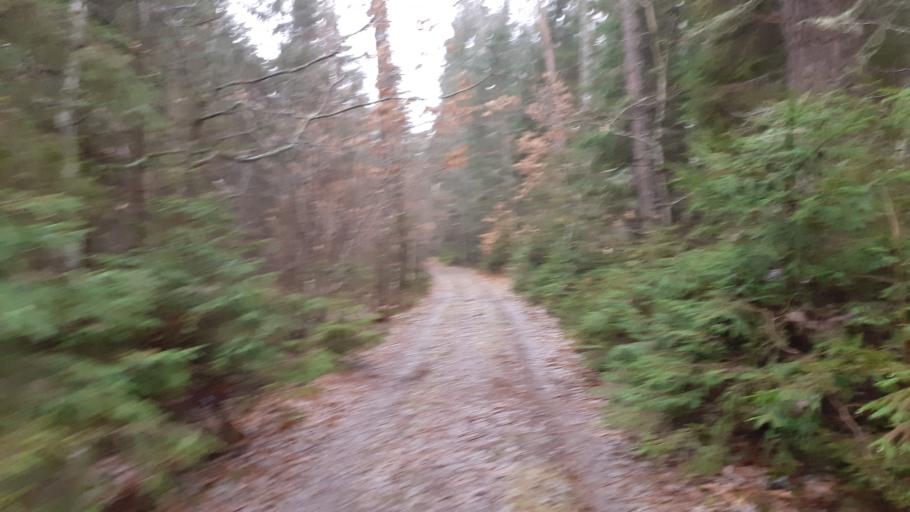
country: LV
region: Kuldigas Rajons
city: Kuldiga
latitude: 57.0024
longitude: 21.9689
